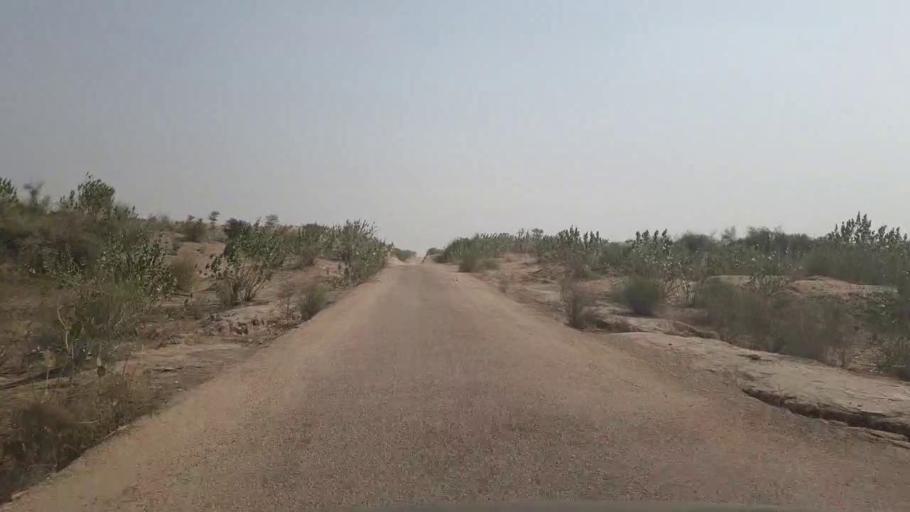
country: PK
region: Sindh
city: Chor
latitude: 25.5927
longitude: 70.0043
